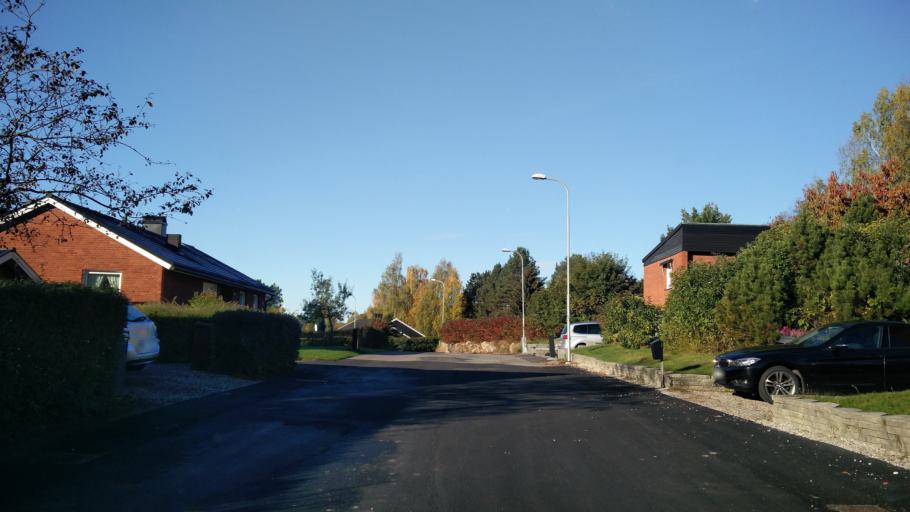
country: SE
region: Vaesternorrland
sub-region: Sundsvalls Kommun
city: Sundsvall
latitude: 62.4072
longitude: 17.2637
